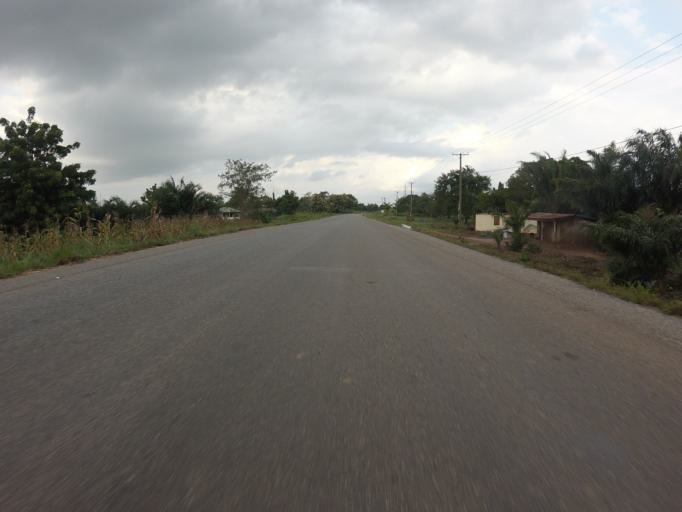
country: GH
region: Volta
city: Ho
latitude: 6.4268
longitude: 0.5138
